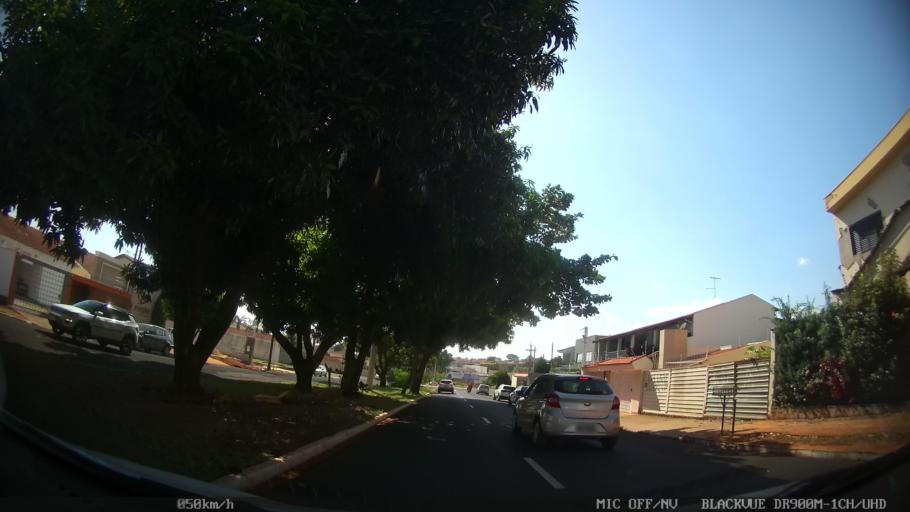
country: BR
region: Sao Paulo
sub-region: Ribeirao Preto
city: Ribeirao Preto
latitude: -21.2077
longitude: -47.8162
